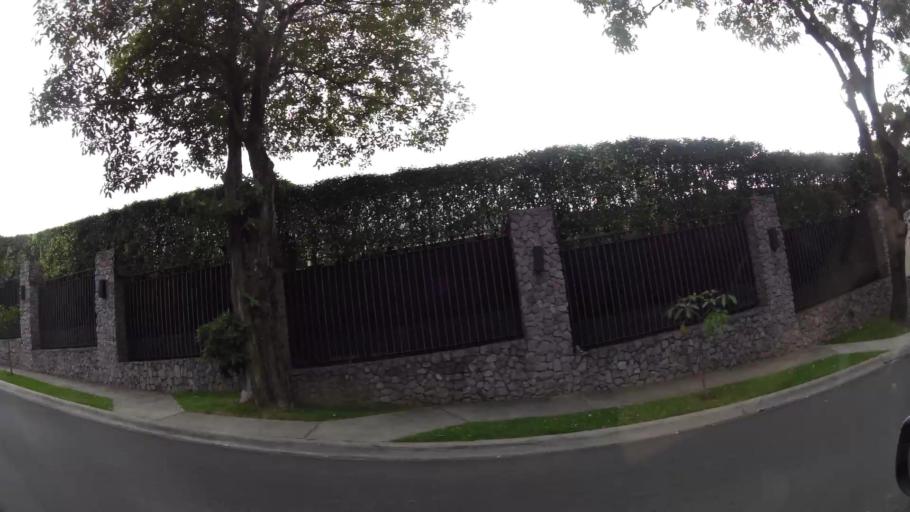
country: CR
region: San Jose
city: San Rafael
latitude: 9.9266
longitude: -84.1462
